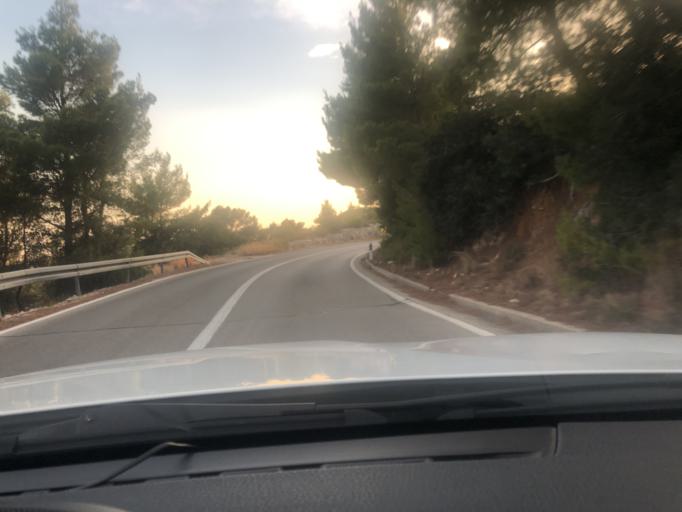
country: HR
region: Splitsko-Dalmatinska
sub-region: Grad Hvar
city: Hvar
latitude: 43.1611
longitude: 16.4955
